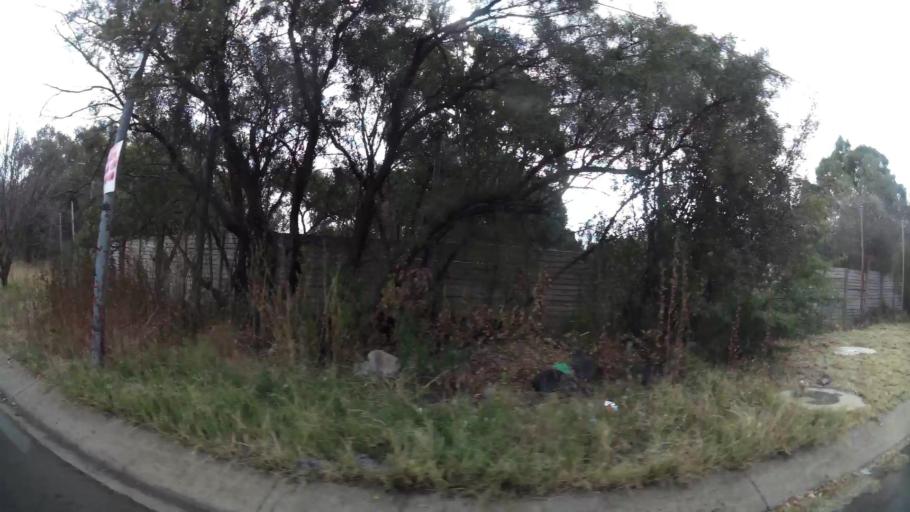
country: ZA
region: Orange Free State
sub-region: Mangaung Metropolitan Municipality
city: Bloemfontein
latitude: -29.0825
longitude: 26.1956
